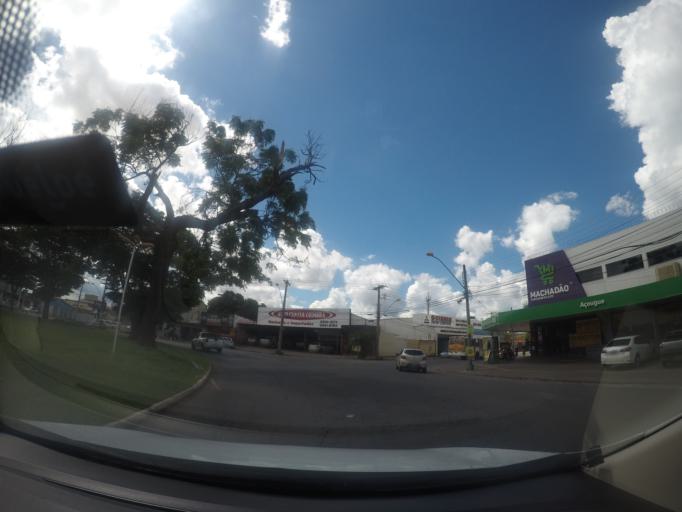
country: BR
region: Goias
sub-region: Goiania
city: Goiania
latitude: -16.6829
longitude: -49.2883
